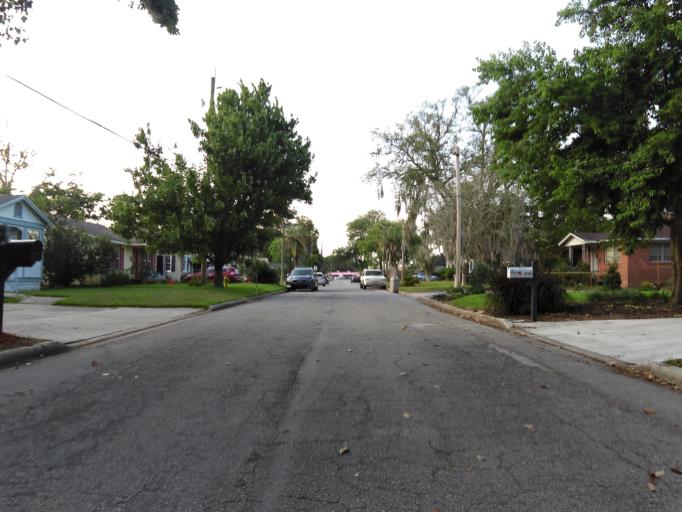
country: US
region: Florida
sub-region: Duval County
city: Jacksonville
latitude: 30.3017
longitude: -81.6310
